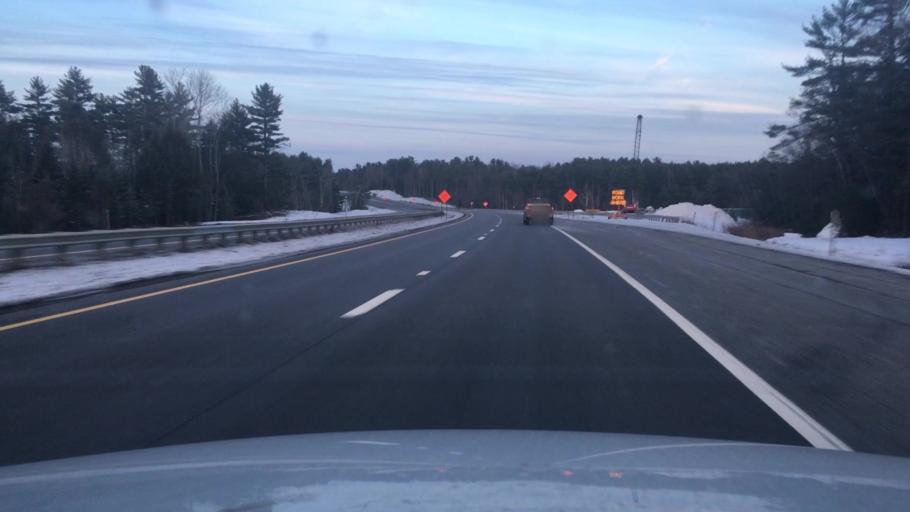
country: US
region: Maine
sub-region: Sagadahoc County
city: Richmond
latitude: 44.1675
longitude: -69.8728
